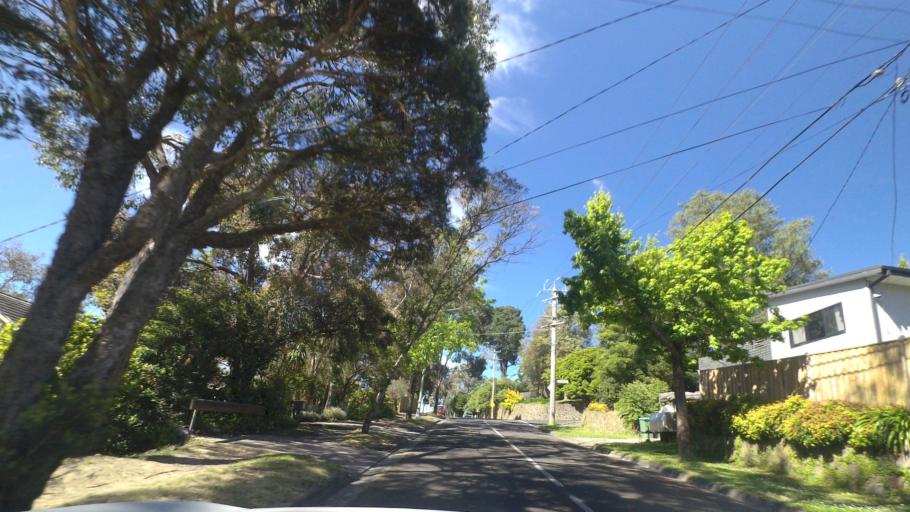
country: AU
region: Victoria
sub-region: Maroondah
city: Ringwood East
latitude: -37.8200
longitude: 145.2580
